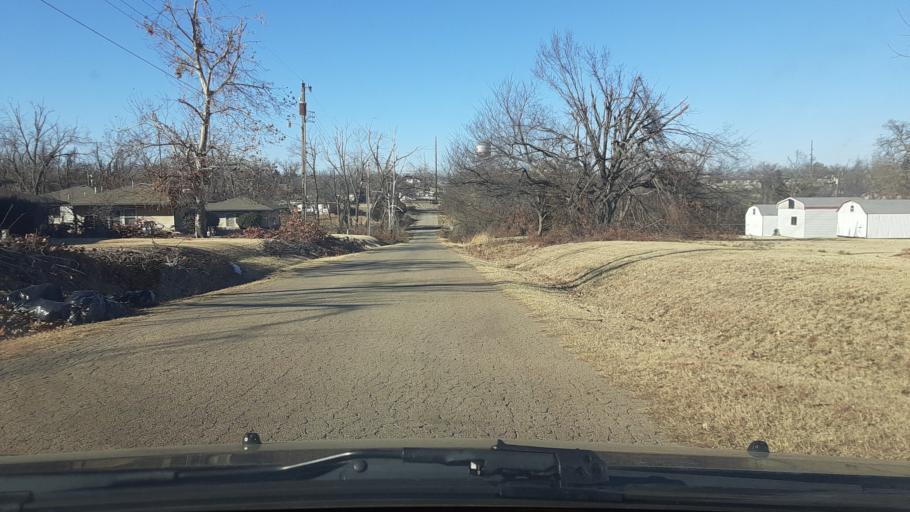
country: US
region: Oklahoma
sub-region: Logan County
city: Guthrie
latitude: 35.8770
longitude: -97.4046
